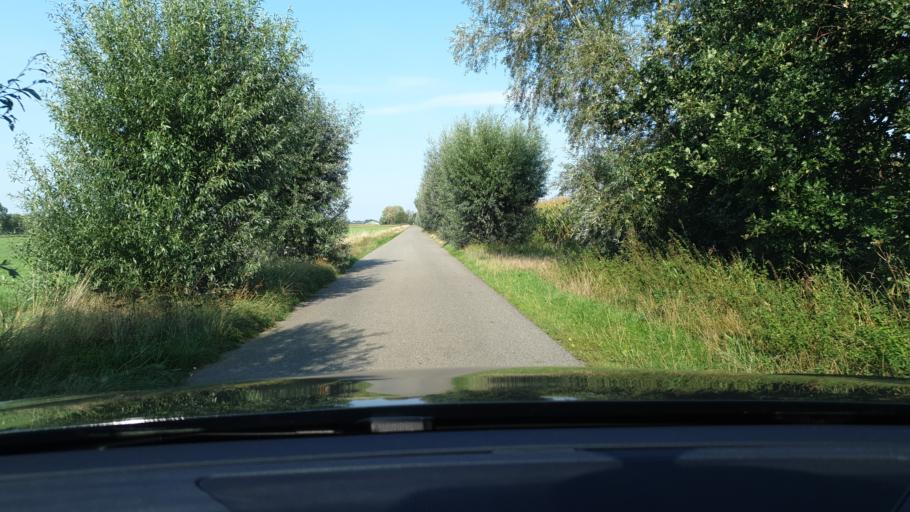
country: NL
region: North Brabant
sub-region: Gemeente Bernheze
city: Loosbroek
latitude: 51.6858
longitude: 5.4769
